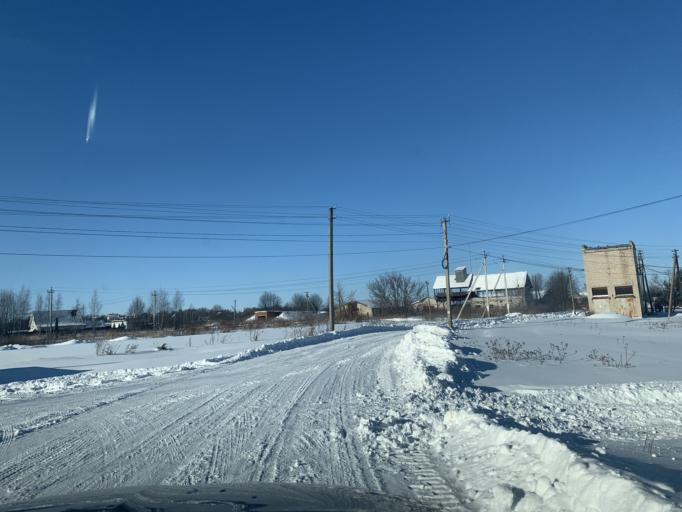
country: RU
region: Jaroslavl
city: Tunoshna
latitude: 57.6602
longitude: 40.0682
